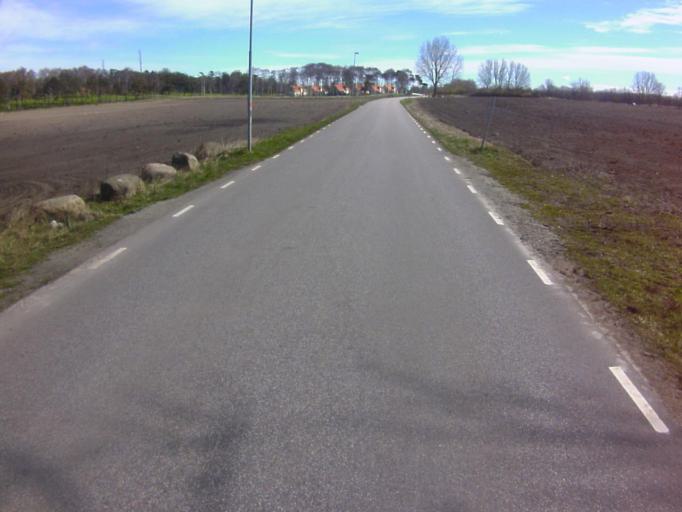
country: SE
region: Skane
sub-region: Kavlinge Kommun
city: Hofterup
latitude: 55.7869
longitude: 12.9419
